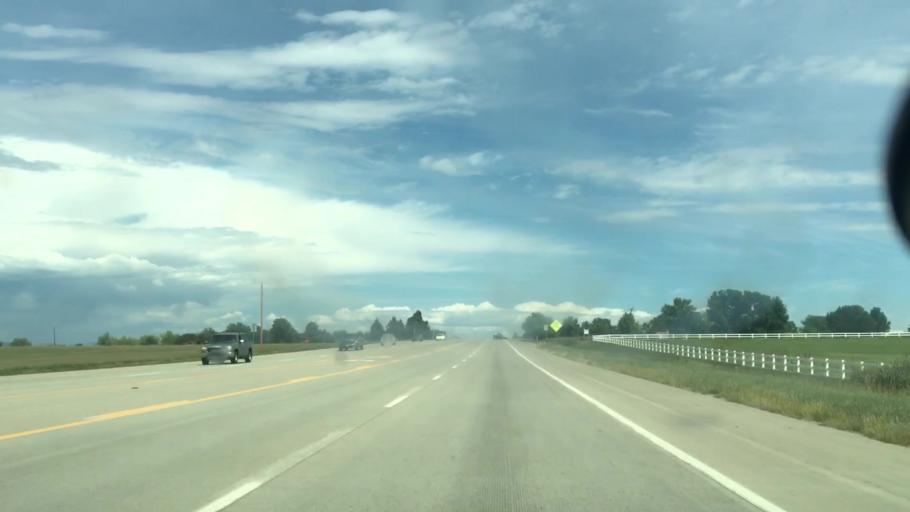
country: US
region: Colorado
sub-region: Boulder County
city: Longmont
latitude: 40.2289
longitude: -105.1023
